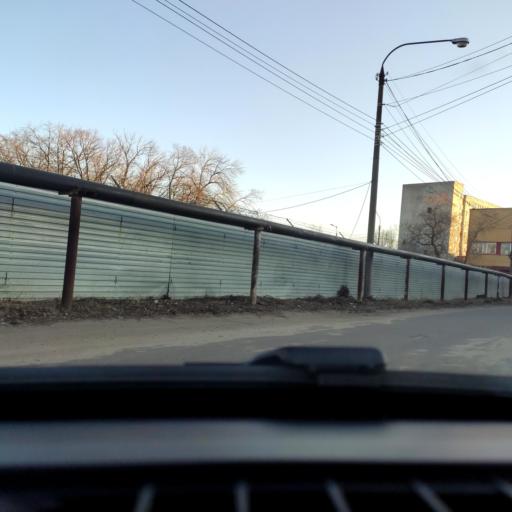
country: RU
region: Voronezj
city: Somovo
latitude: 51.6738
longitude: 39.2962
